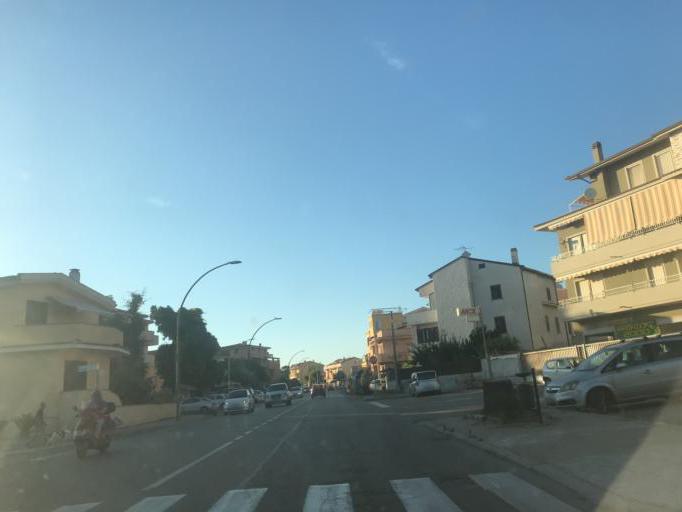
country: IT
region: Sardinia
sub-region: Provincia di Sassari
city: Alghero
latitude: 40.5813
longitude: 8.3183
